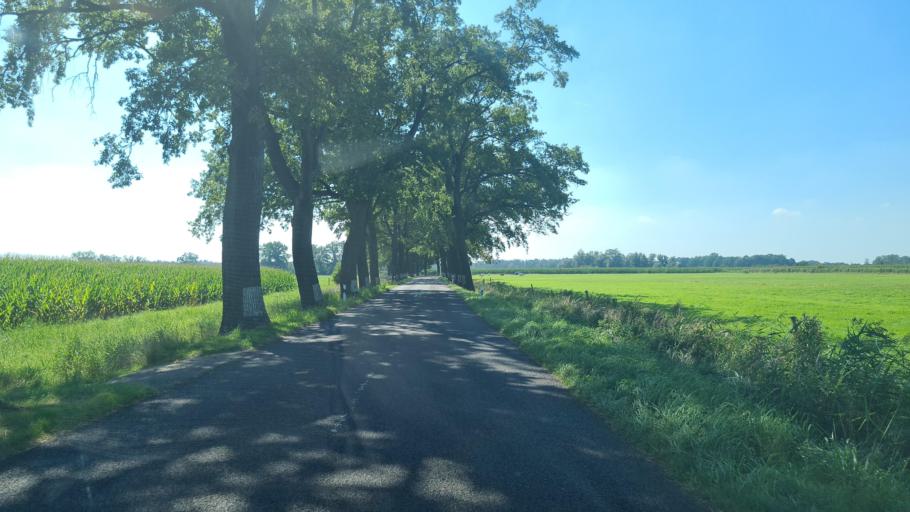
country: DE
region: Brandenburg
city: Paulinenaue
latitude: 52.6551
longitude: 12.7030
